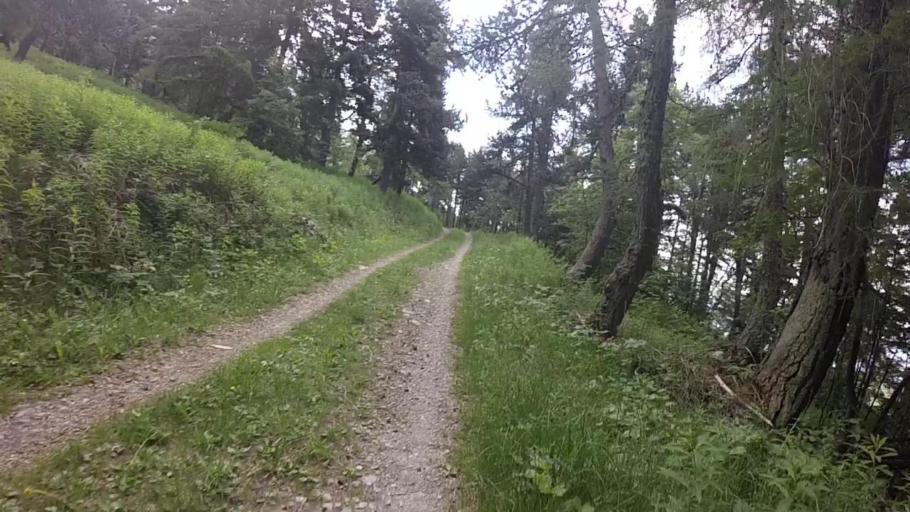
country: FR
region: Provence-Alpes-Cote d'Azur
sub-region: Departement des Alpes-de-Haute-Provence
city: Seyne-les-Alpes
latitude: 44.4032
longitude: 6.3760
